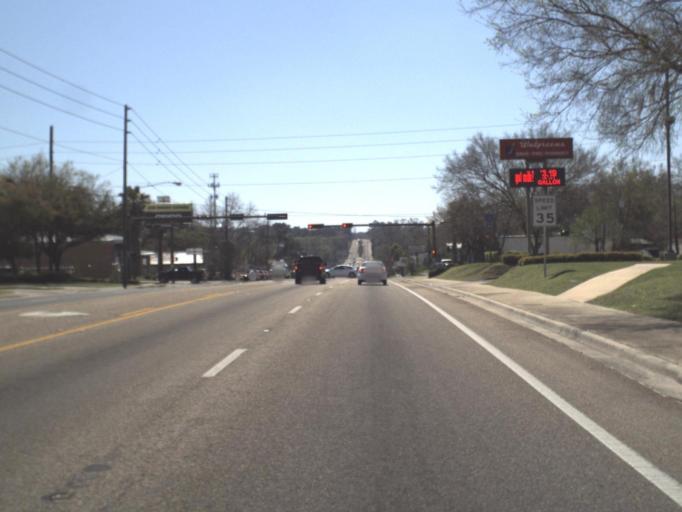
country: US
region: Florida
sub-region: Leon County
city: Tallahassee
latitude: 30.4209
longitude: -84.2807
